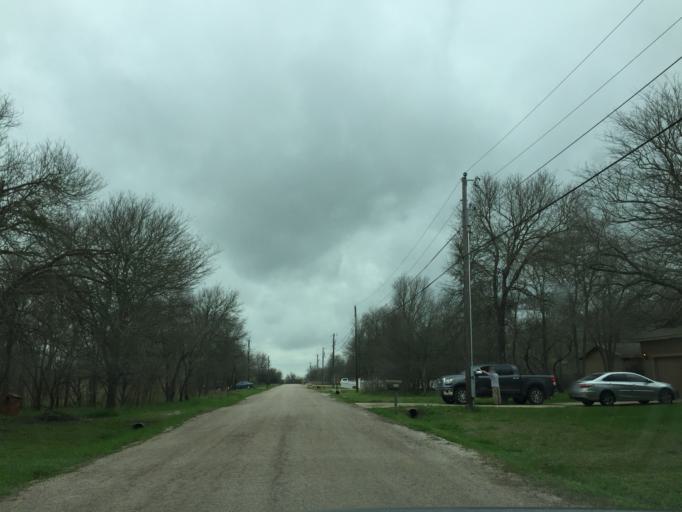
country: US
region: Texas
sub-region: Bastrop County
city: Bastrop
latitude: 30.0848
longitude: -97.3167
